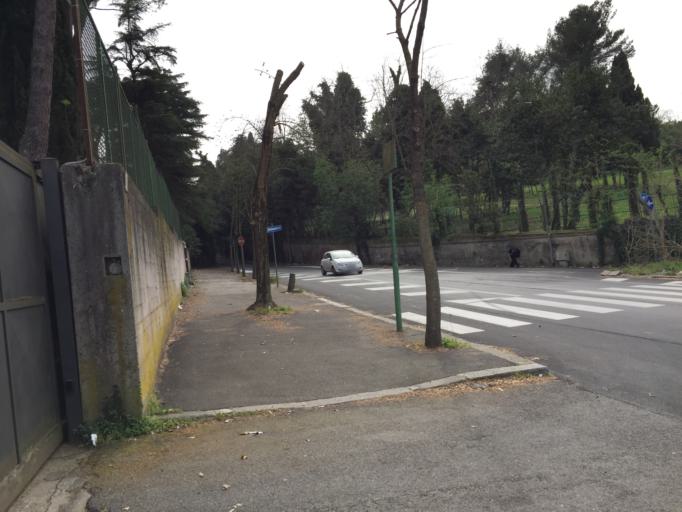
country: VA
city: Vatican City
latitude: 41.8911
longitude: 12.4585
